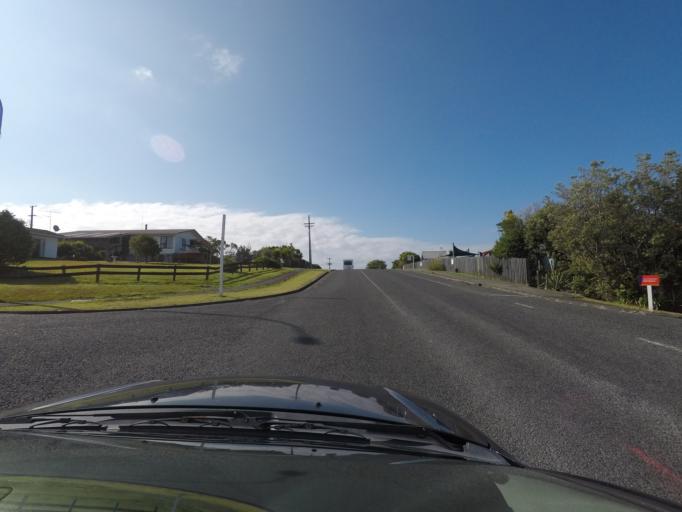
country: NZ
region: Auckland
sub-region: Auckland
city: Warkworth
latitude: -36.2919
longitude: 174.8033
